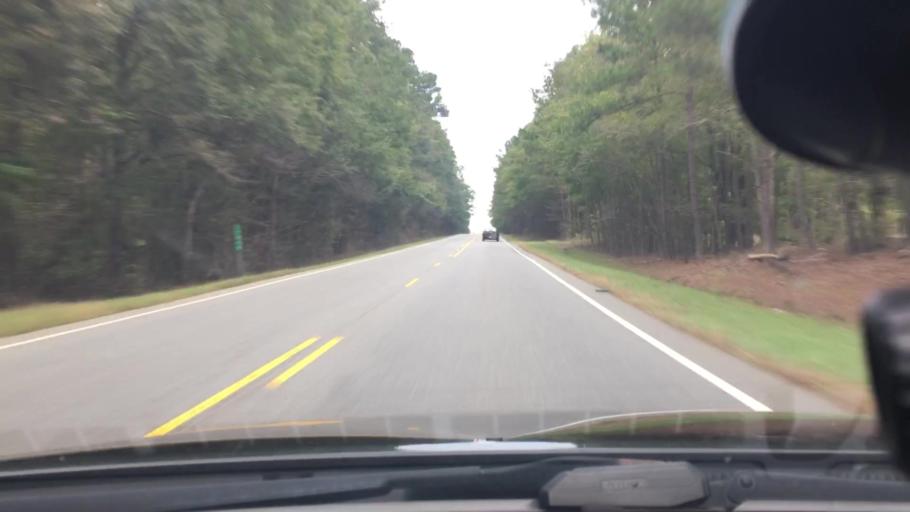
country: US
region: North Carolina
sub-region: Montgomery County
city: Biscoe
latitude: 35.3621
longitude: -79.6916
